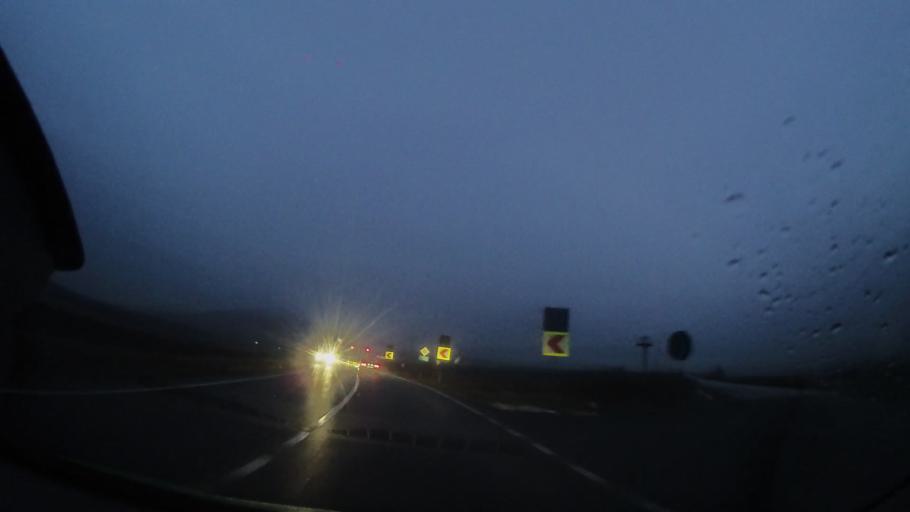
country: RO
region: Harghita
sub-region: Comuna Ditrau
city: Ditrau
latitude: 46.8320
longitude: 25.4923
